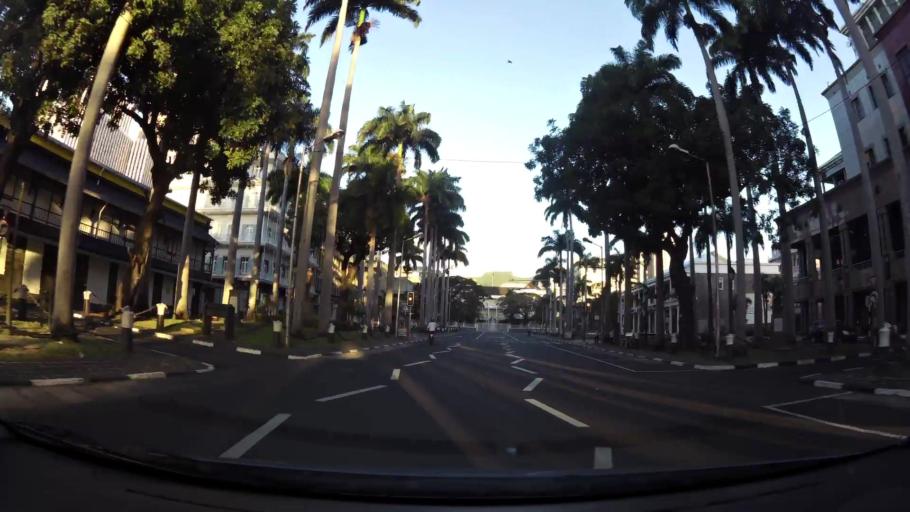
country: MU
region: Port Louis
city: Port Louis
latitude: -20.1617
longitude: 57.5021
